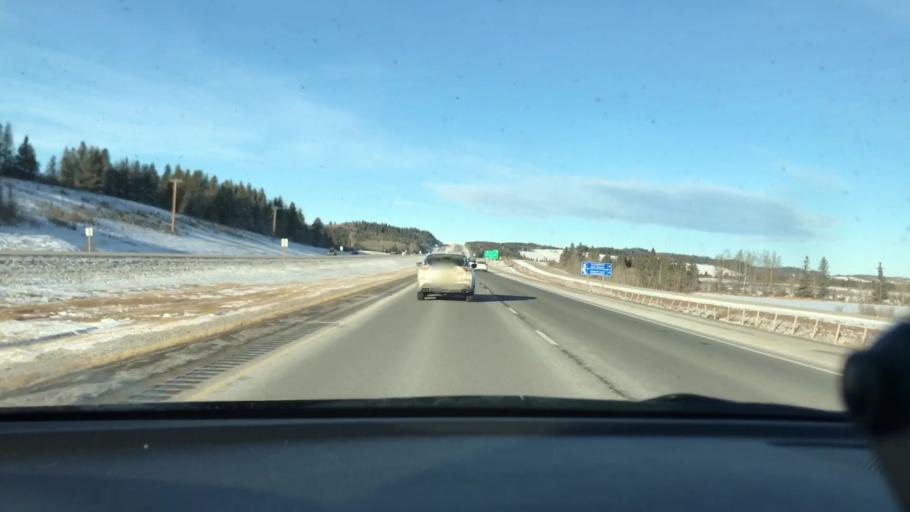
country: CA
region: Alberta
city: Cochrane
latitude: 51.1272
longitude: -114.6838
